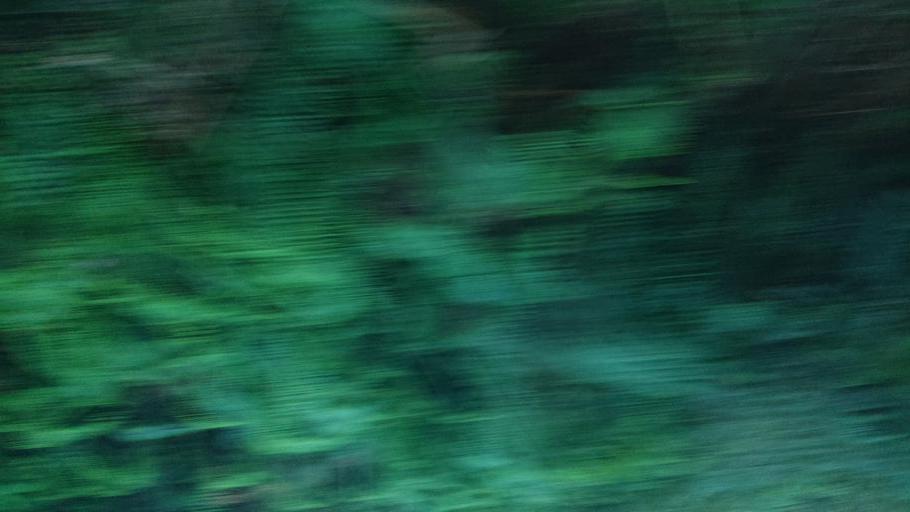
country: TW
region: Taiwan
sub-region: Yunlin
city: Douliu
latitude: 23.5311
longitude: 120.6577
